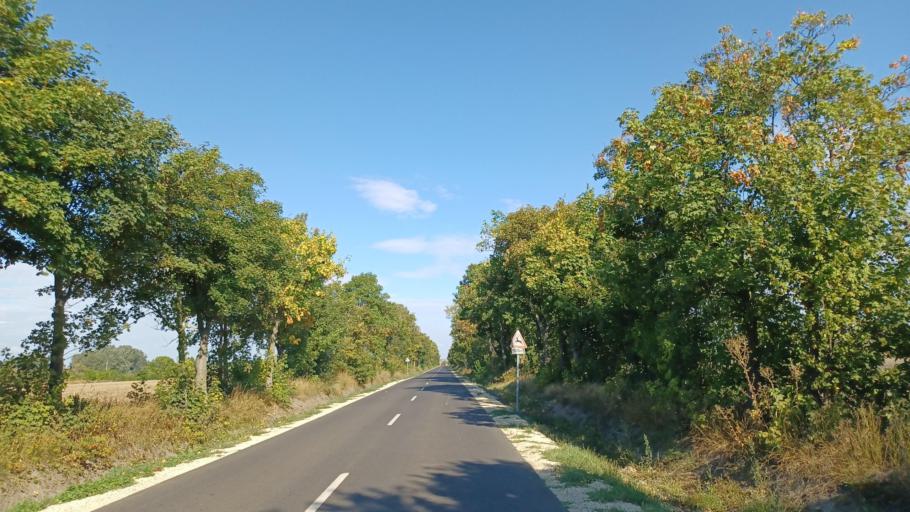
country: HU
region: Tolna
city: Dunaszentgyorgy
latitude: 46.4992
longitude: 18.8280
